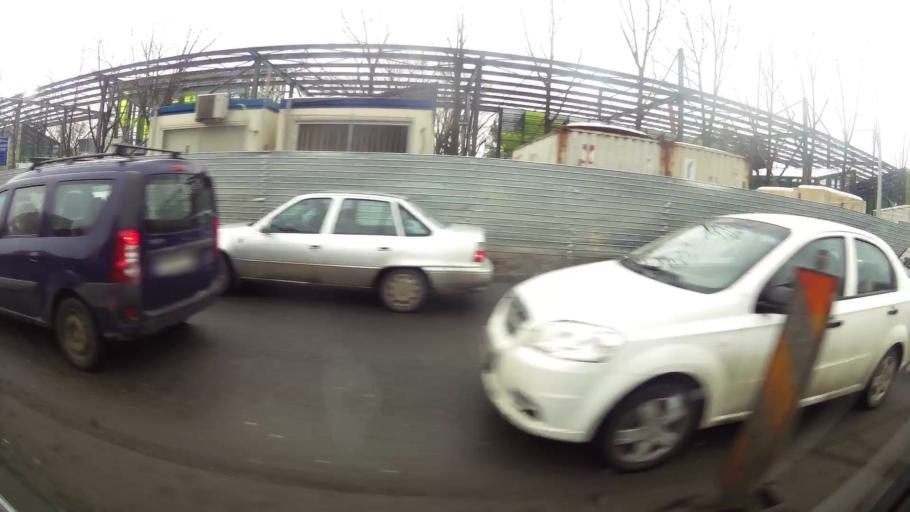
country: RO
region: Ilfov
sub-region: Comuna Chiajna
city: Rosu
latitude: 44.4221
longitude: 26.0321
